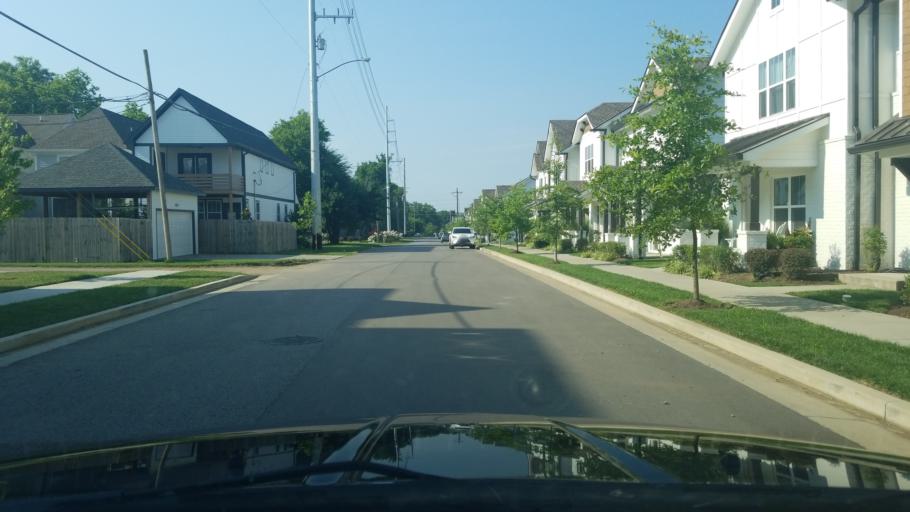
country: US
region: Tennessee
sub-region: Davidson County
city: Belle Meade
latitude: 36.1637
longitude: -86.8570
